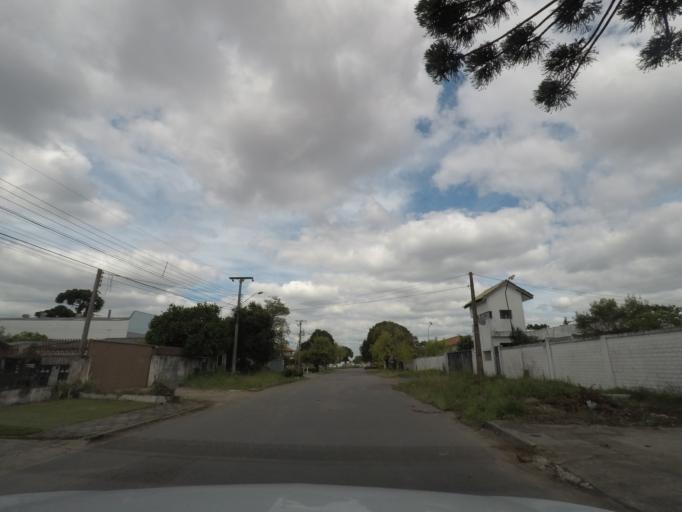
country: BR
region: Parana
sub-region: Sao Jose Dos Pinhais
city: Sao Jose dos Pinhais
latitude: -25.4926
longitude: -49.2365
